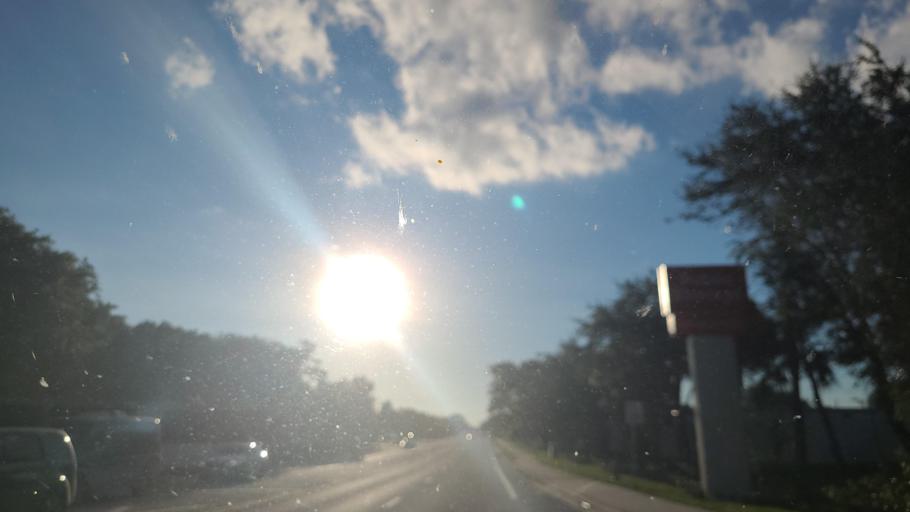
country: US
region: Florida
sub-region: Indian River County
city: Florida Ridge
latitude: 27.6089
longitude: -80.3851
